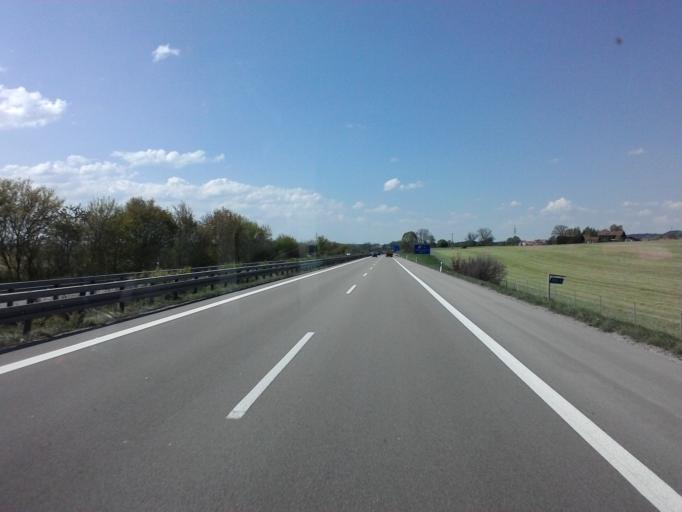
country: DE
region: Bavaria
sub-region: Swabia
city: Lauben
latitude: 47.8001
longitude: 10.3146
